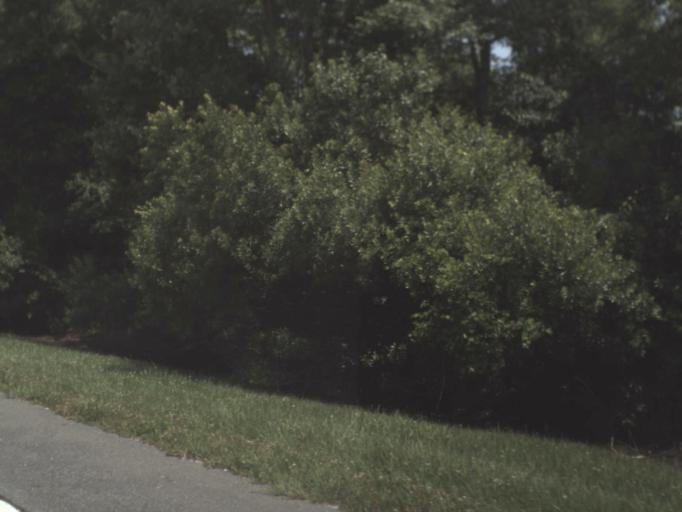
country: US
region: Florida
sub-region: Duval County
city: Baldwin
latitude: 30.2051
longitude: -81.9854
